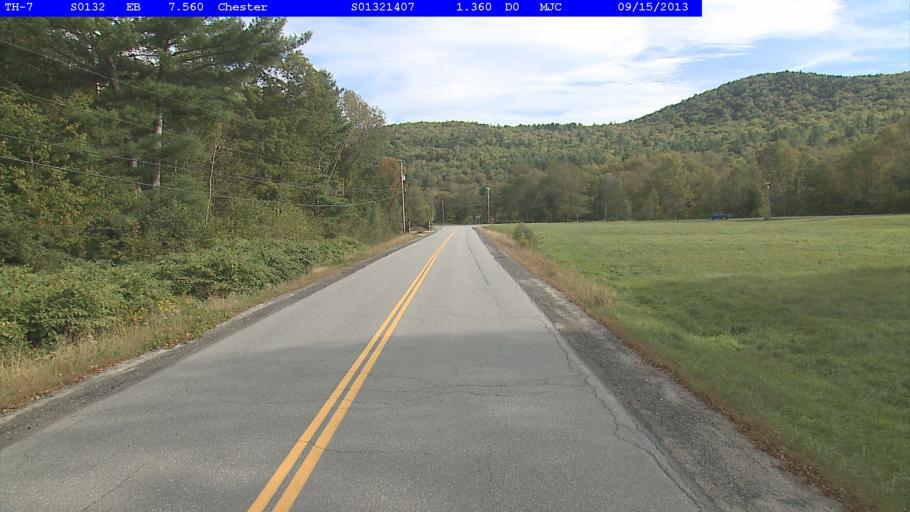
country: US
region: Vermont
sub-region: Windsor County
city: Chester
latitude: 43.2636
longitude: -72.6624
